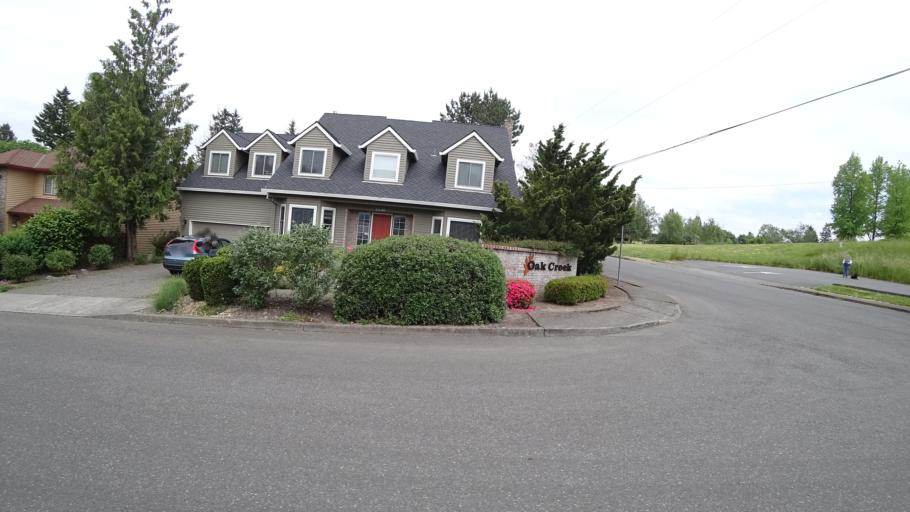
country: US
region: Oregon
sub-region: Clackamas County
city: Lake Oswego
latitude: 45.4410
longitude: -122.7053
